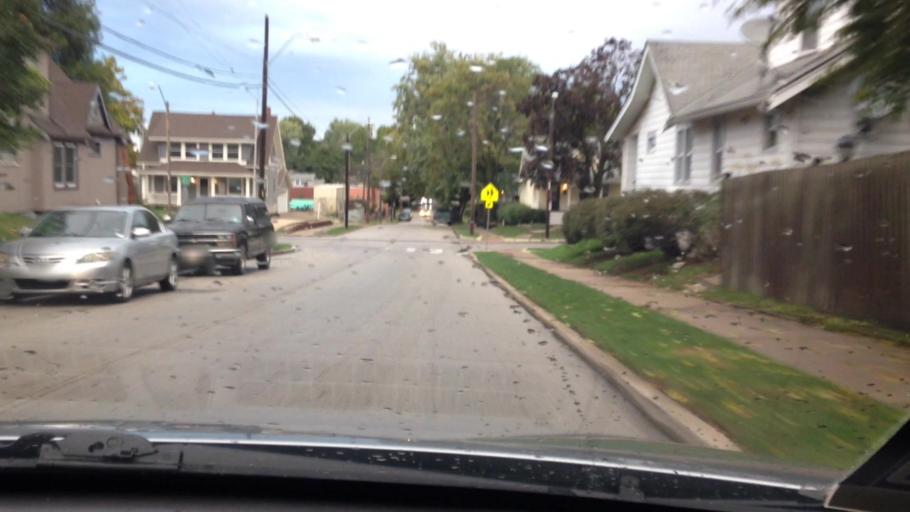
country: US
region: Kansas
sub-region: Johnson County
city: Mission Hills
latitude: 38.9928
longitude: -94.5918
